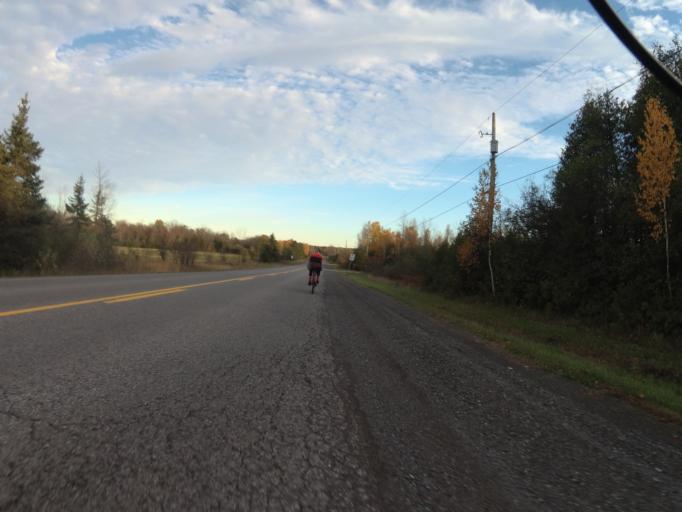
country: CA
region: Ontario
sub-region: Lanark County
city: Smiths Falls
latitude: 44.9822
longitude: -75.7950
